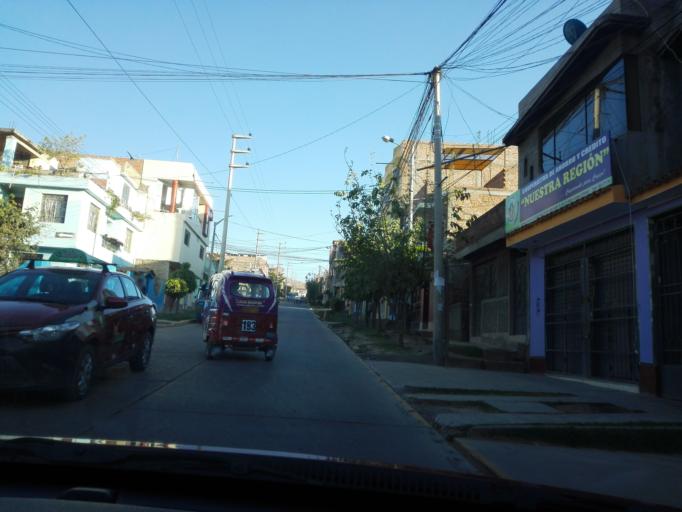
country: PE
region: Ayacucho
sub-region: Provincia de Huamanga
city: Ayacucho
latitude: -13.1480
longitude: -74.2283
